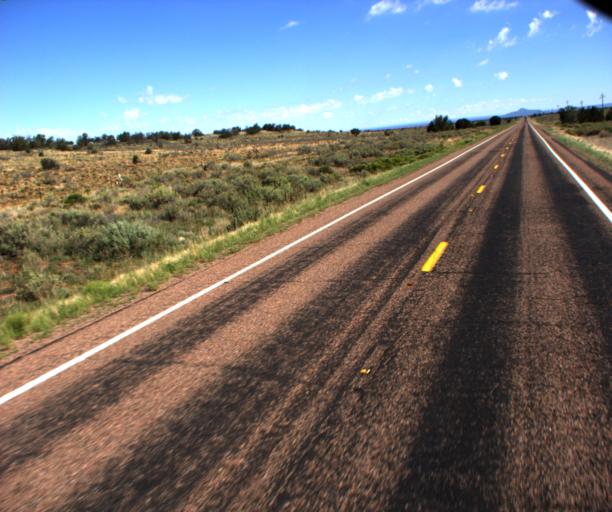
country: US
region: Arizona
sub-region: Coconino County
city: Williams
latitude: 35.5700
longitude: -112.1552
